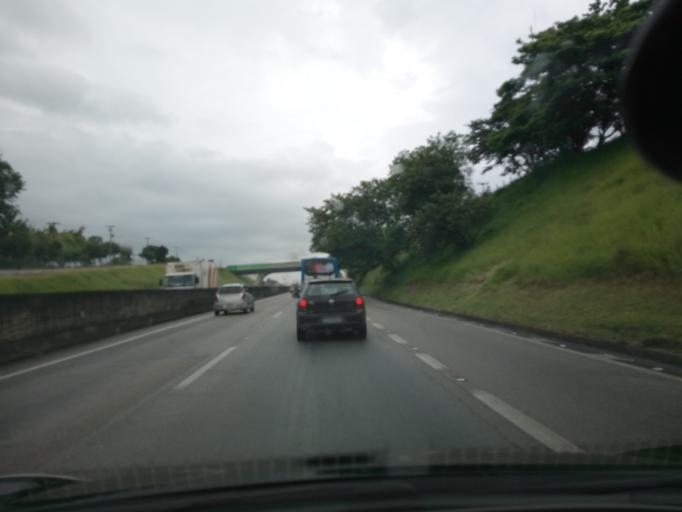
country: BR
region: Sao Paulo
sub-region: Campinas
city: Campinas
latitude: -22.9716
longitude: -47.1021
